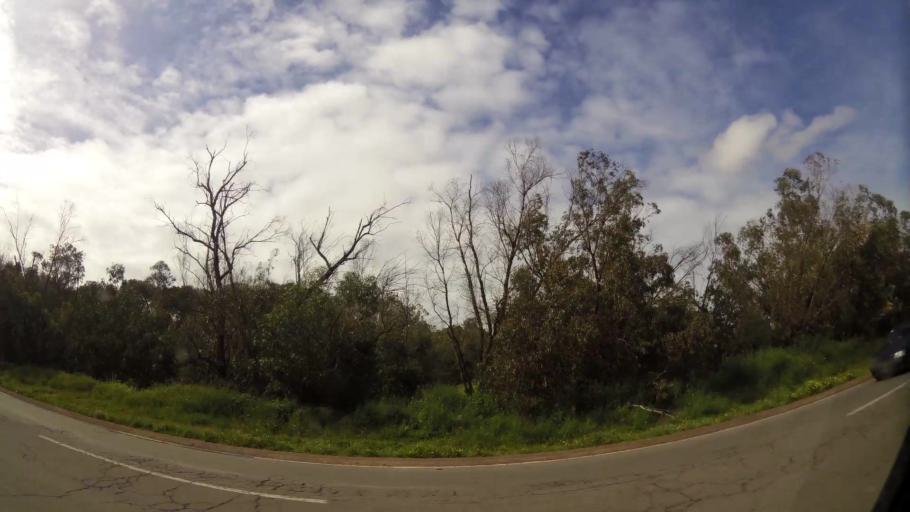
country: MA
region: Grand Casablanca
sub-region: Mohammedia
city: Mohammedia
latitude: 33.6518
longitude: -7.4056
